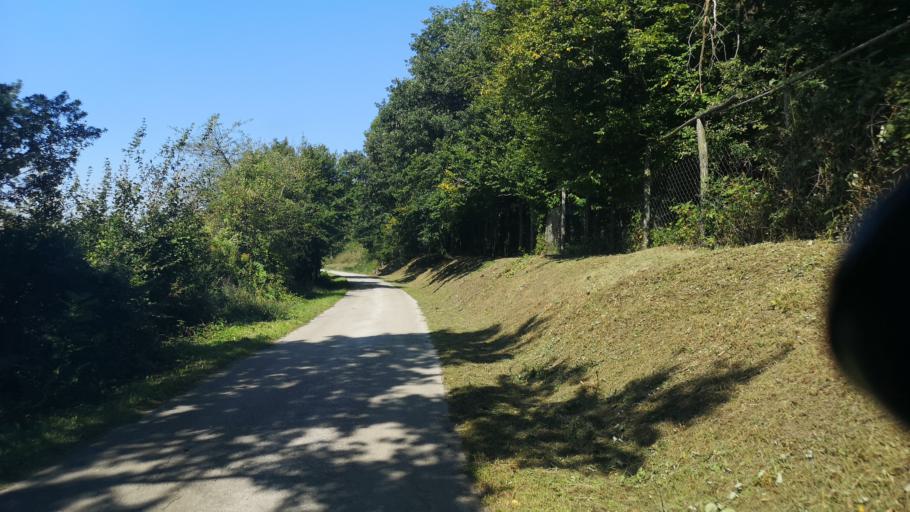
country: SK
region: Trnavsky
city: Smolenice
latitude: 48.5736
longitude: 17.4168
